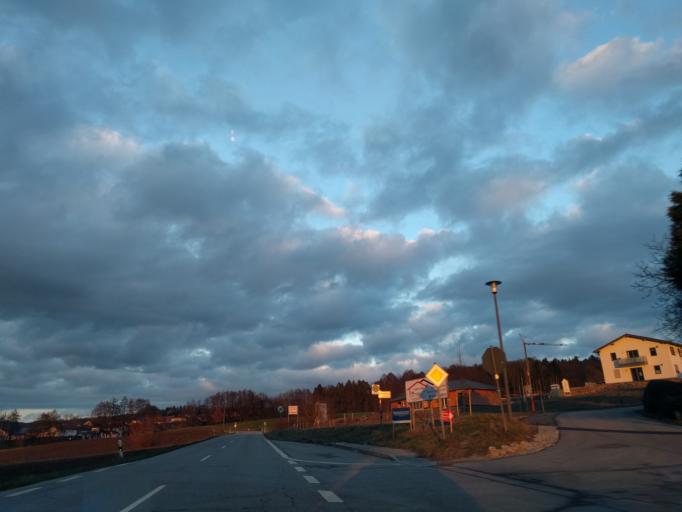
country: DE
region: Bavaria
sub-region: Lower Bavaria
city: Hofkirchen
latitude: 48.6890
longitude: 13.1193
